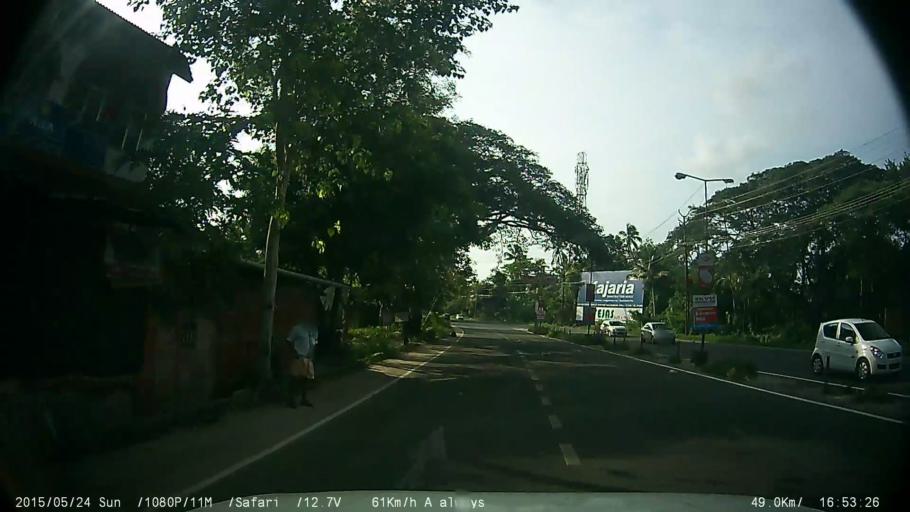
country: IN
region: Kerala
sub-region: Alappuzha
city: Shertallai
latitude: 9.6739
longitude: 76.3399
